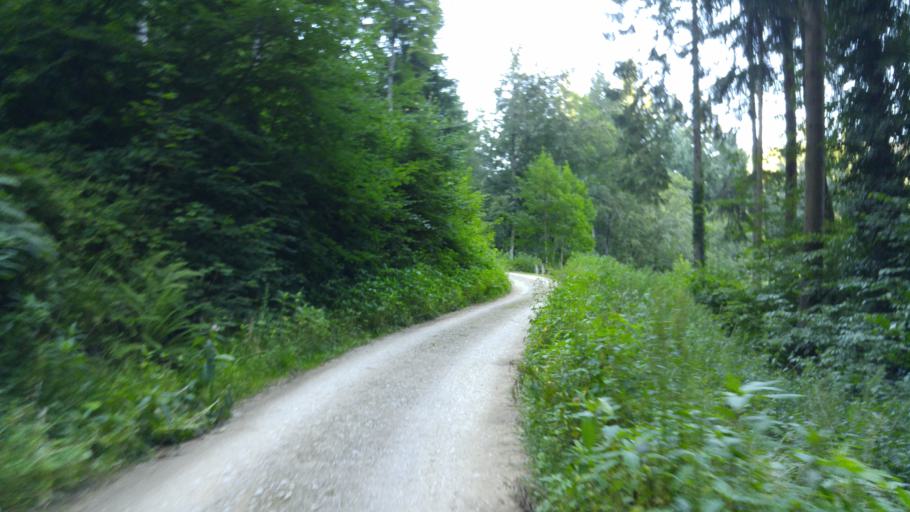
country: DE
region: Baden-Wuerttemberg
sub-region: Freiburg Region
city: Muenstertal/Schwarzwald
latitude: 47.8403
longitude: 7.7906
